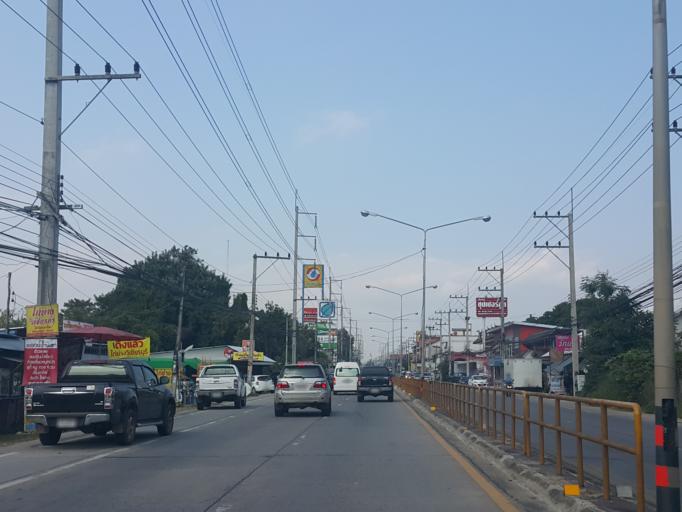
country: TH
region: Chiang Mai
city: San Sai
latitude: 18.8991
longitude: 98.9510
